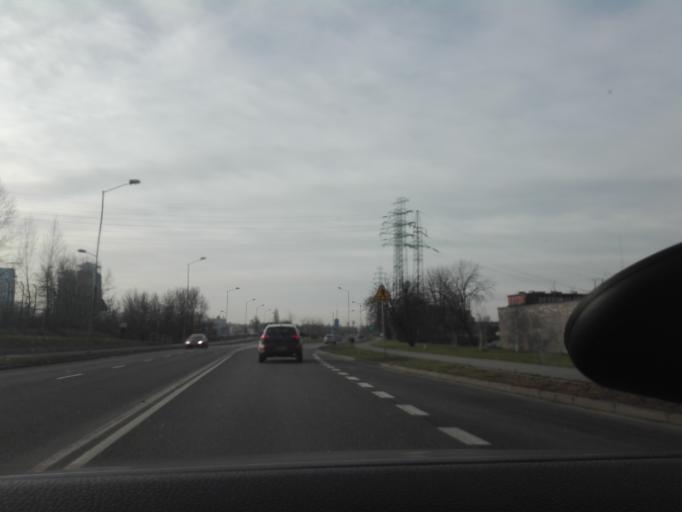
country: PL
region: Silesian Voivodeship
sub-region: Katowice
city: Katowice
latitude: 50.2704
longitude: 19.0153
